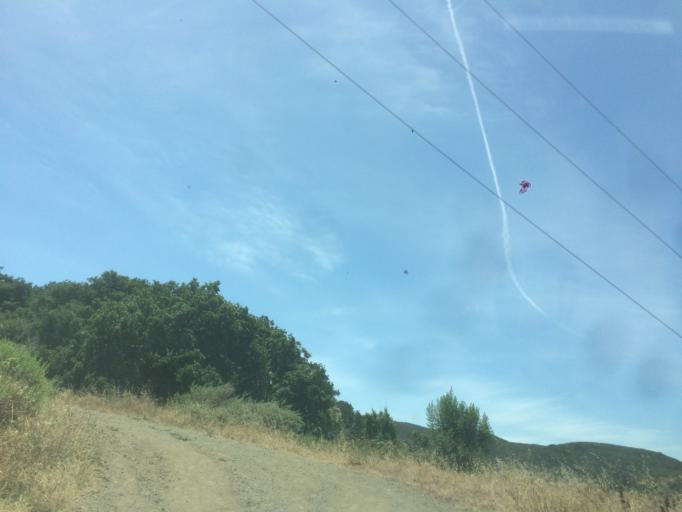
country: US
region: California
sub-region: San Luis Obispo County
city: San Luis Obispo
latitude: 35.2542
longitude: -120.7034
